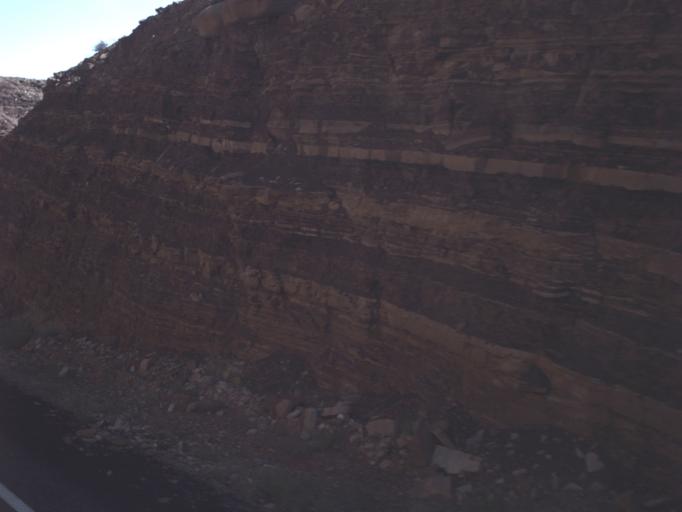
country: US
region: Utah
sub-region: San Juan County
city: Blanding
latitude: 37.8898
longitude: -110.4135
